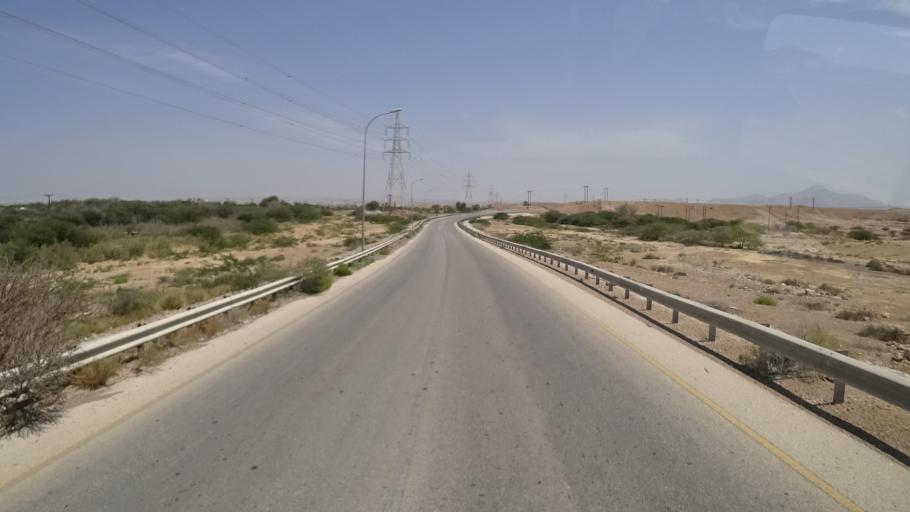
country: OM
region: Ash Sharqiyah
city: Sur
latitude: 22.5844
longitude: 59.4566
